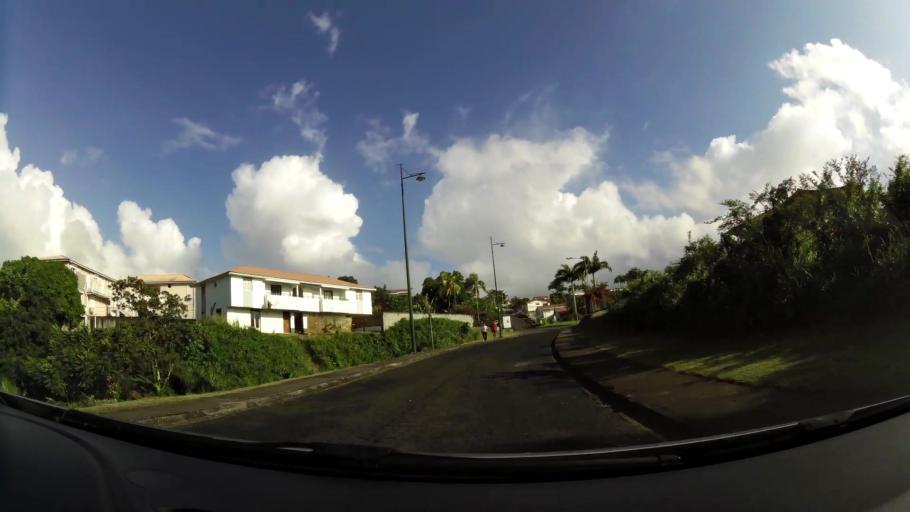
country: MQ
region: Martinique
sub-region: Martinique
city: Ducos
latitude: 14.5734
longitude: -60.9706
